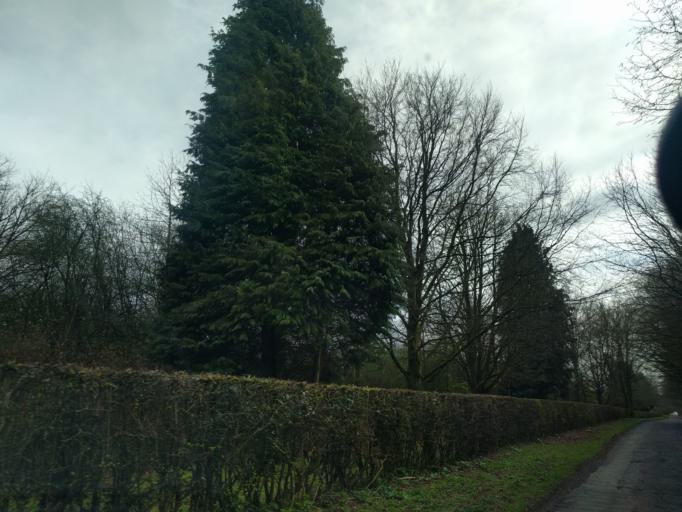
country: GB
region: England
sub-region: Wiltshire
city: Colerne
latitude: 51.4469
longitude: -2.2888
